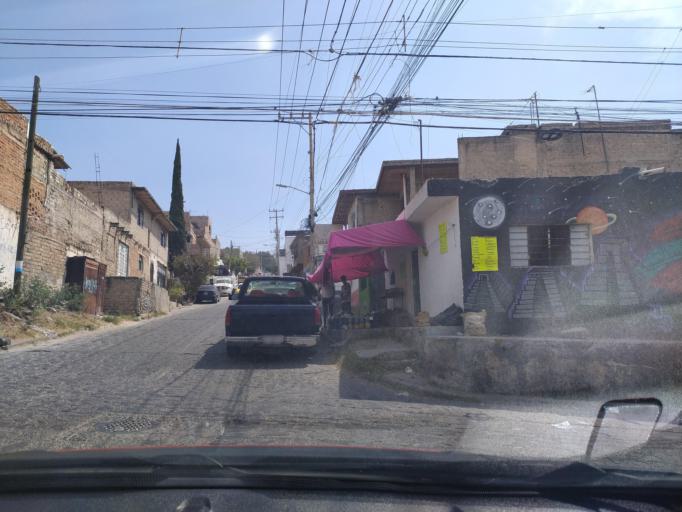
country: MX
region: Jalisco
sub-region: Tlajomulco de Zuniga
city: Altus Bosques
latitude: 20.6107
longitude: -103.3688
